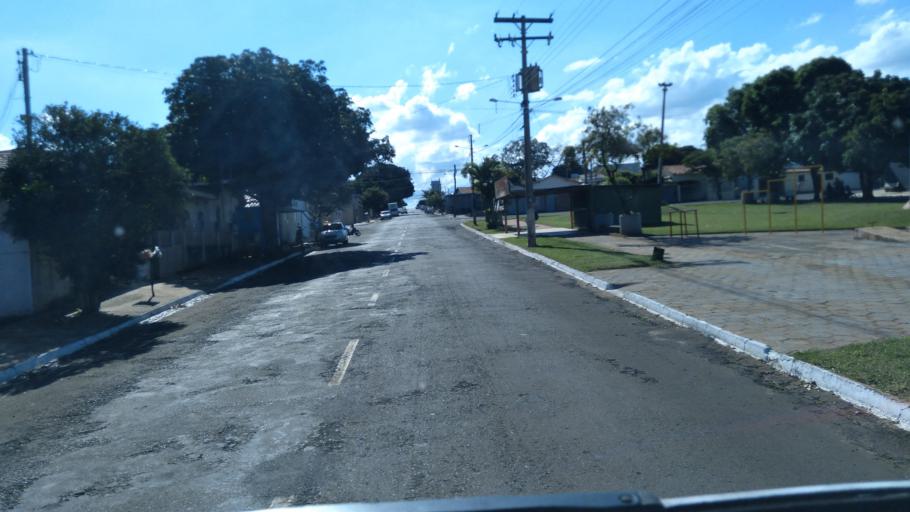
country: BR
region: Goias
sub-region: Mineiros
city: Mineiros
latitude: -17.5596
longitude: -52.5517
